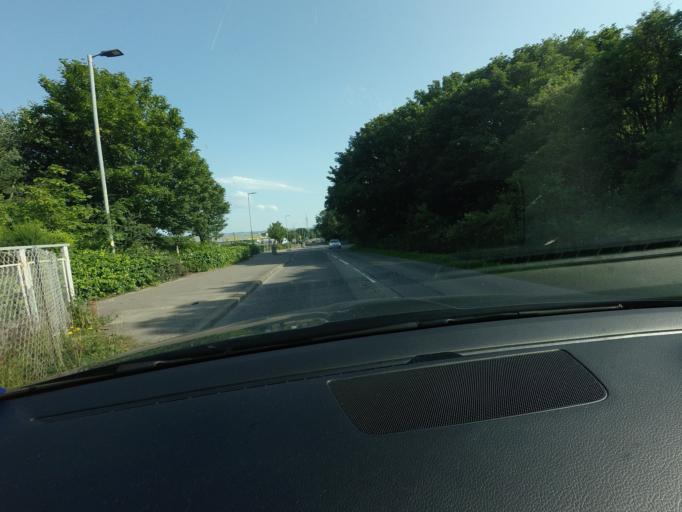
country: GB
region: Scotland
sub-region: Highland
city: Alness
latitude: 57.6937
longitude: -4.2447
